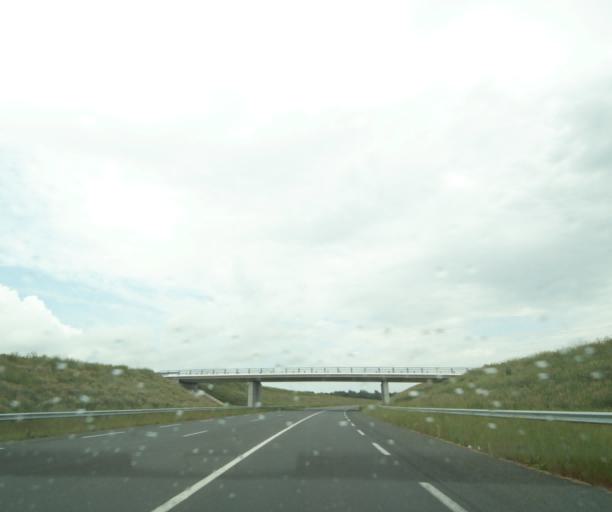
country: FR
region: Poitou-Charentes
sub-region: Departement des Deux-Sevres
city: Louzy
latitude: 47.0546
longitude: -0.1946
